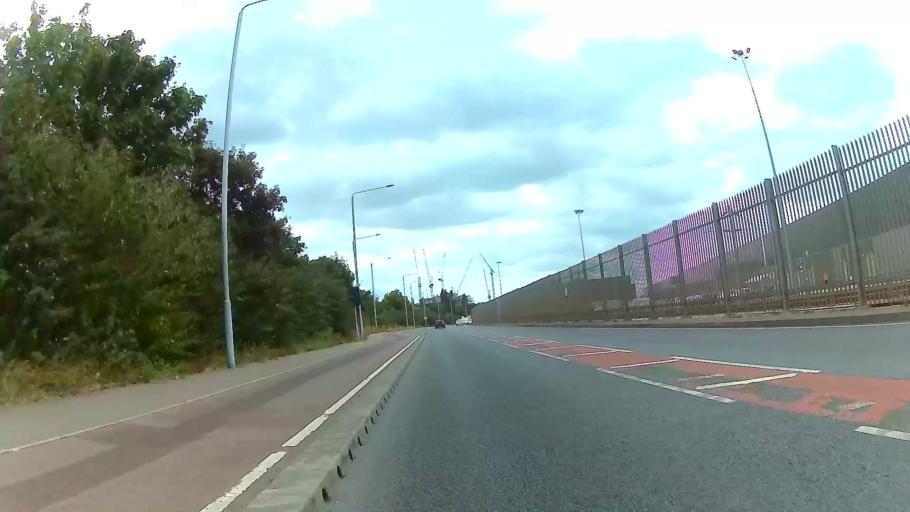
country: GB
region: England
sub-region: Greater London
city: Hackney
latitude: 51.5619
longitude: -0.0252
